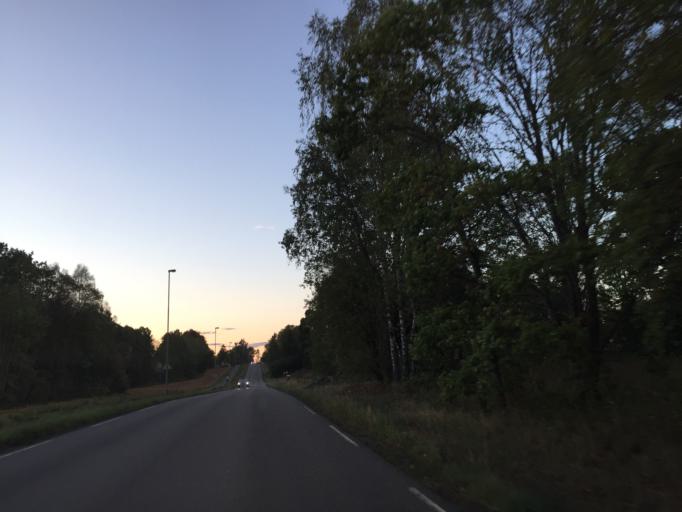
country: NO
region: Ostfold
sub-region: Moss
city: Moss
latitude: 59.4966
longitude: 10.6877
